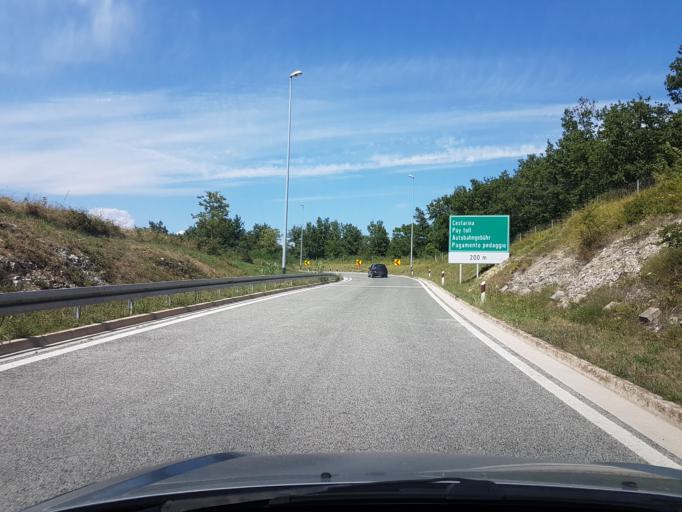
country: HR
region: Istarska
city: Buje
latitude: 45.4008
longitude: 13.6235
